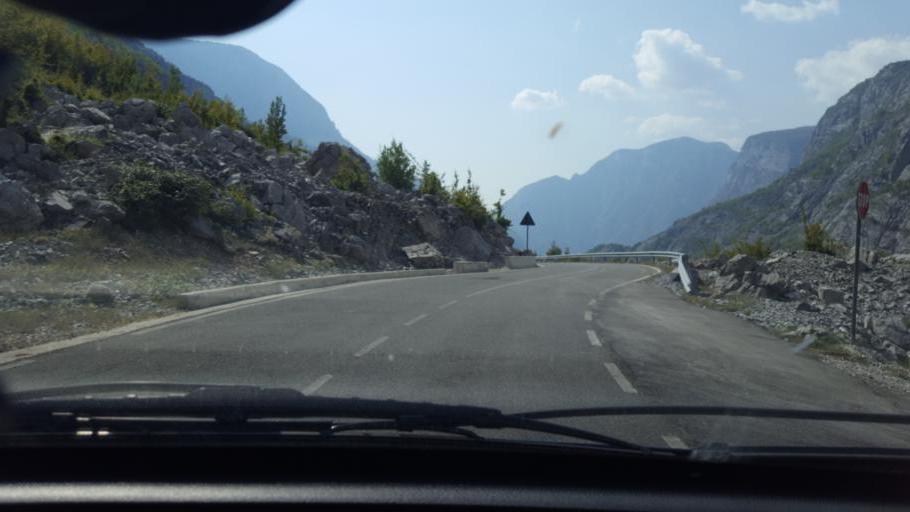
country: AL
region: Shkoder
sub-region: Rrethi i Malesia e Madhe
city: Kastrat
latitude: 42.5192
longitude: 19.6271
